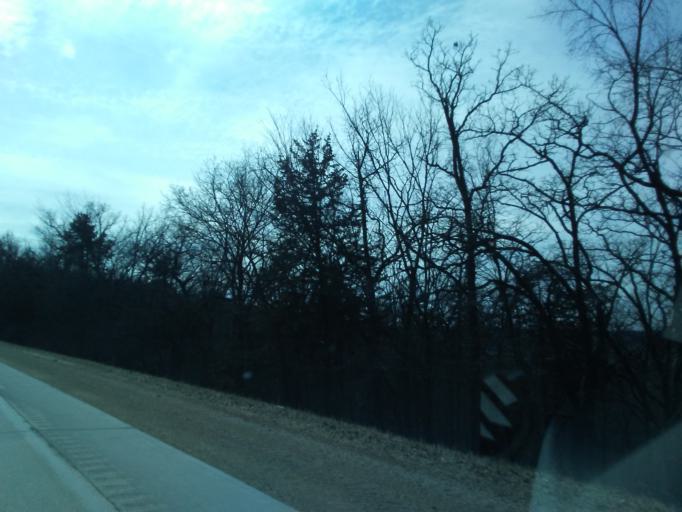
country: US
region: Iowa
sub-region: Winneshiek County
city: Decorah
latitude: 43.3403
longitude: -91.8114
